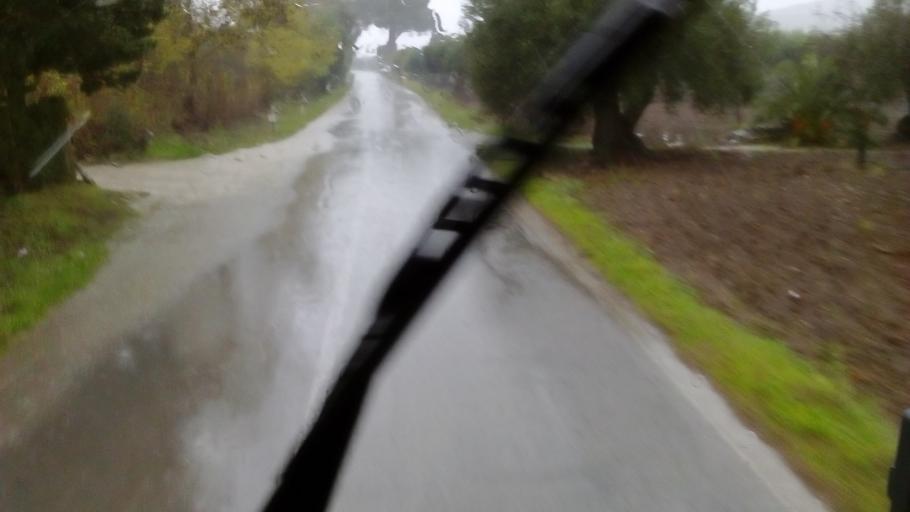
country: IT
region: Sicily
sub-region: Enna
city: Pietraperzia
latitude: 37.4205
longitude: 14.1673
